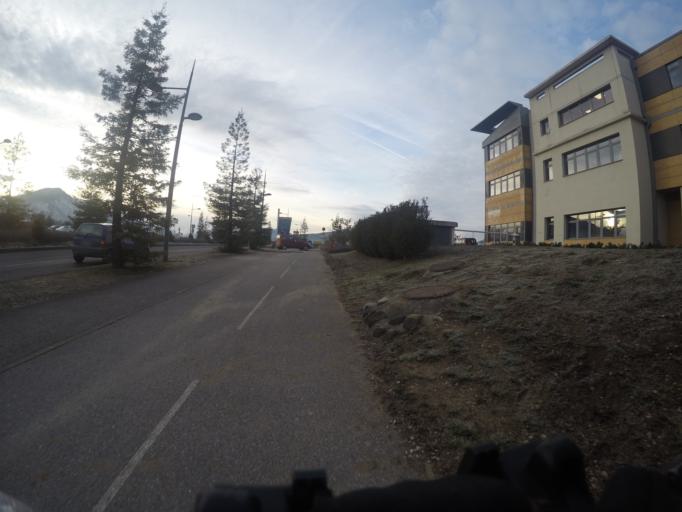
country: FR
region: Rhone-Alpes
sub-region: Departement de la Haute-Savoie
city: Metz-Tessy
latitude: 45.9355
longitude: 6.1174
